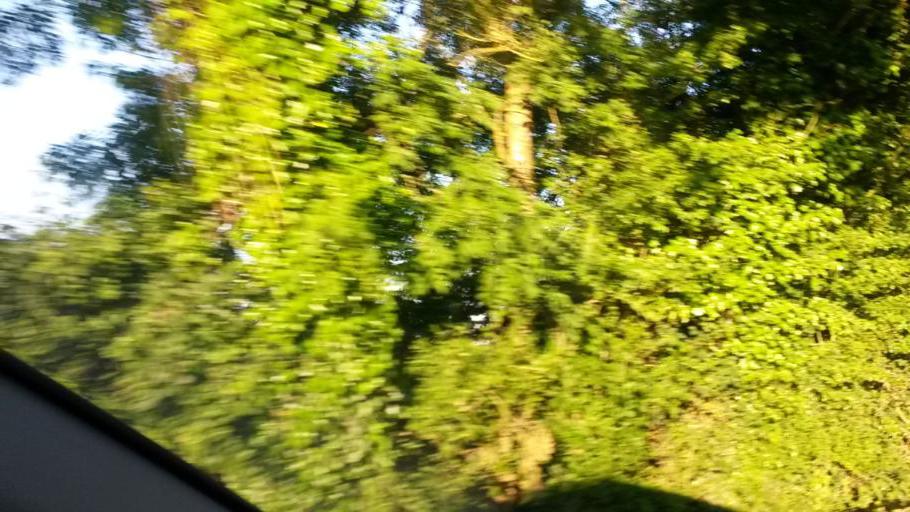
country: IE
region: Leinster
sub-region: An Mhi
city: Ashbourne
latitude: 53.5486
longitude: -6.3594
